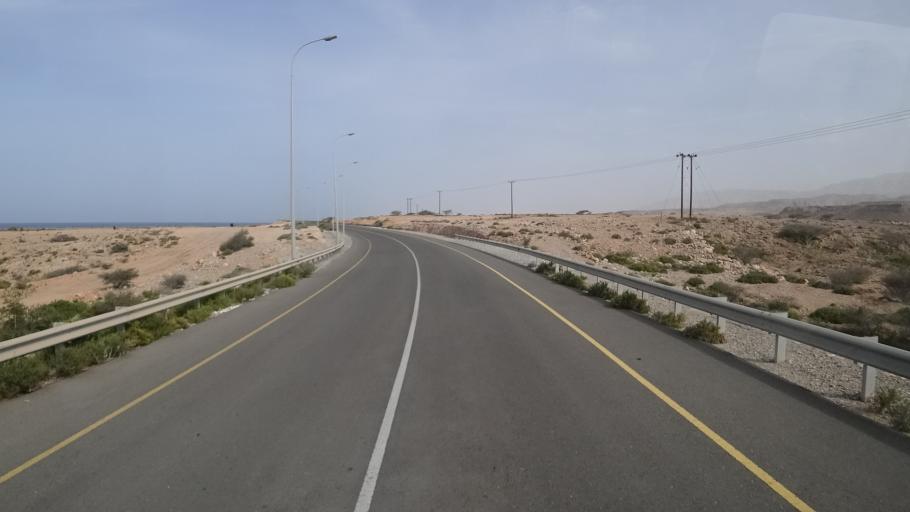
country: OM
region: Ash Sharqiyah
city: Al Qabil
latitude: 23.0058
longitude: 59.1135
